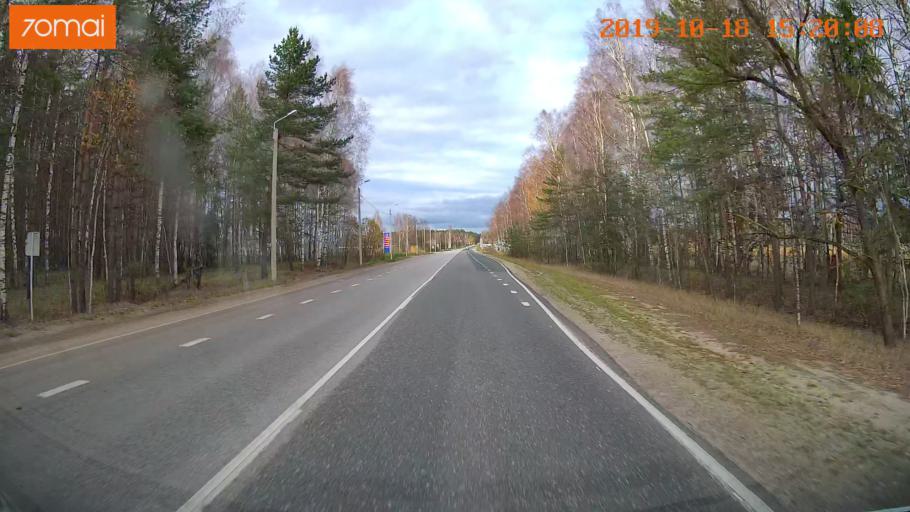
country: RU
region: Vladimir
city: Anopino
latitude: 55.6833
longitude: 40.7428
